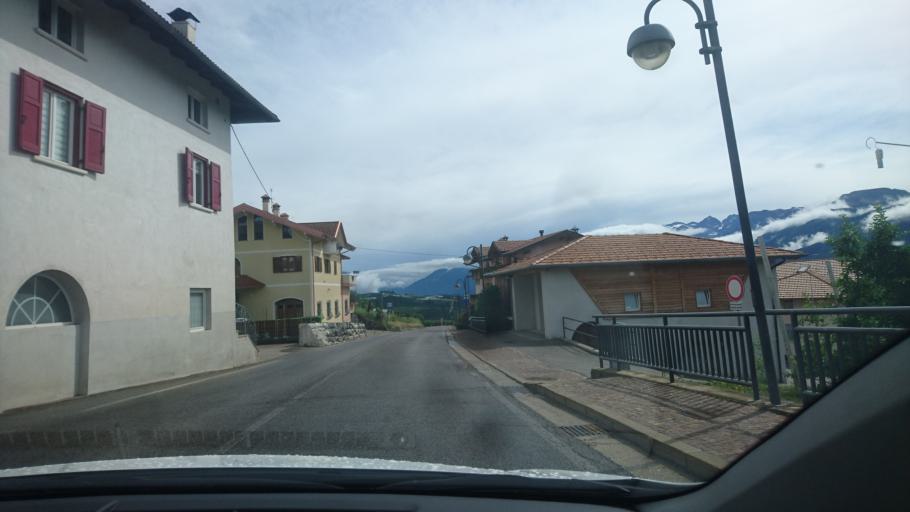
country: IT
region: Trentino-Alto Adige
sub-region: Provincia di Trento
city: Sanzeno
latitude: 46.3790
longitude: 11.0891
